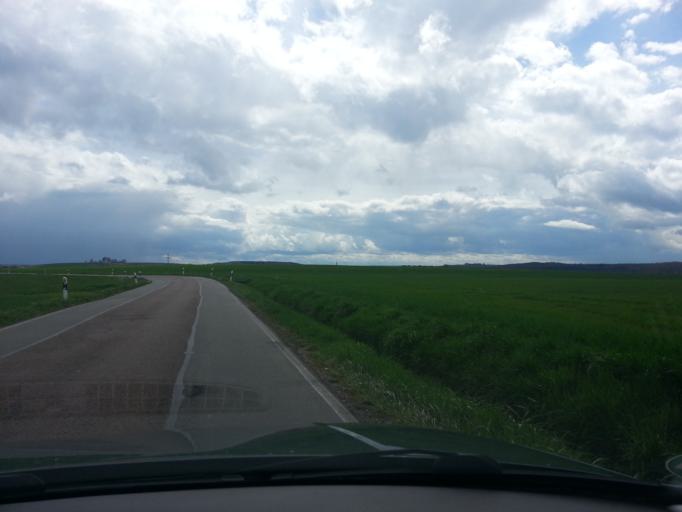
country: DE
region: Rheinland-Pfalz
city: Schmitshausen
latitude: 49.2995
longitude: 7.5117
